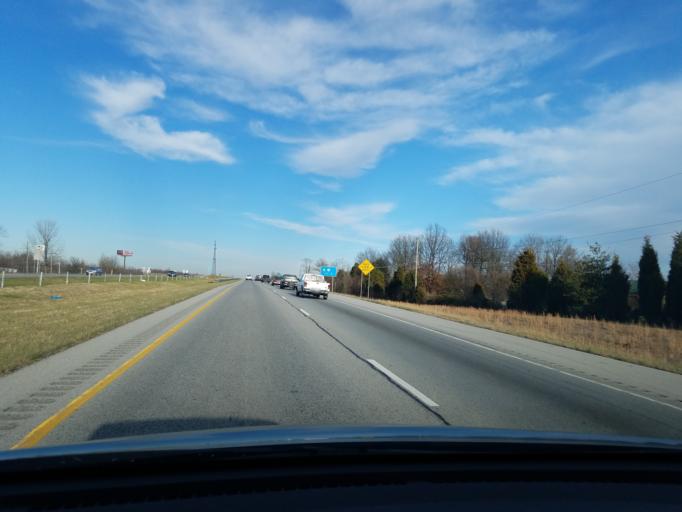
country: US
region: Indiana
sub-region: Floyd County
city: New Albany
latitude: 38.3307
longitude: -85.8273
